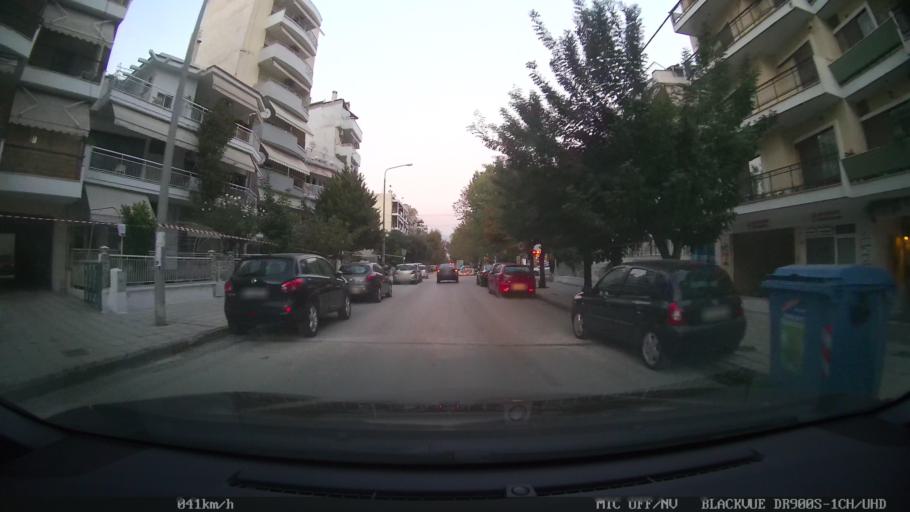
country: GR
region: Central Macedonia
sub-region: Nomos Thessalonikis
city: Kalamaria
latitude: 40.5825
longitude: 22.9551
